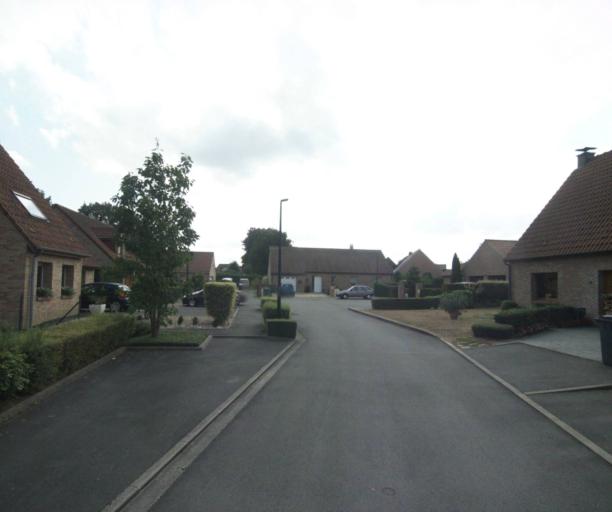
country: FR
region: Nord-Pas-de-Calais
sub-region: Departement du Nord
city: Lys-lez-Lannoy
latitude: 50.6635
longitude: 3.2194
